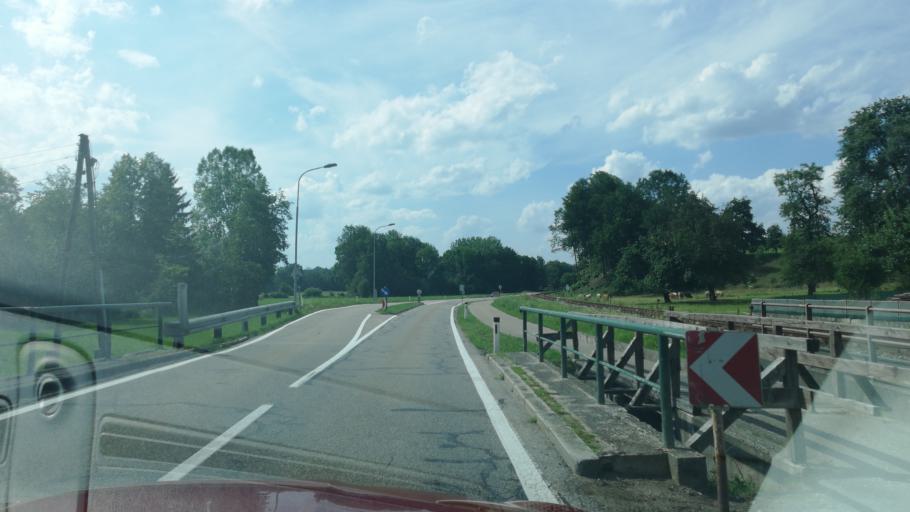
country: AT
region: Upper Austria
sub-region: Politischer Bezirk Vocklabruck
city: Puhret
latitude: 48.0236
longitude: 13.7093
